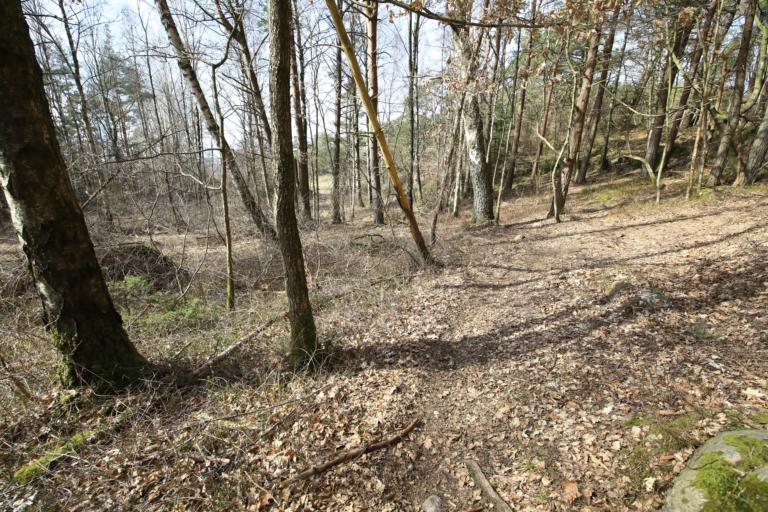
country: SE
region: Halland
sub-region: Varbergs Kommun
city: Varberg
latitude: 57.1475
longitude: 12.2847
